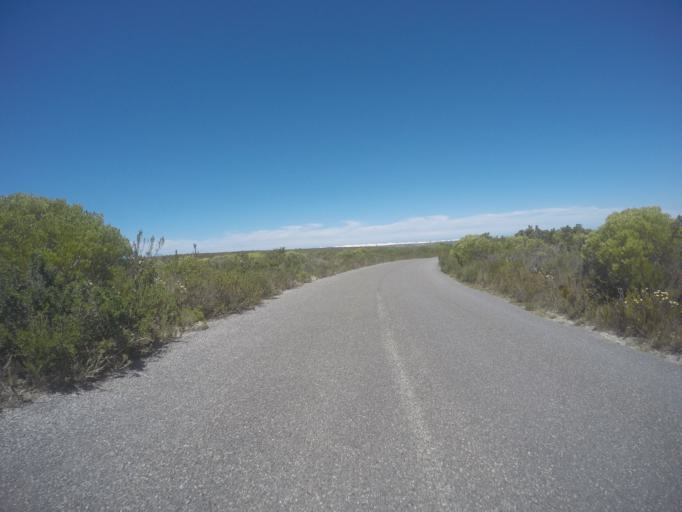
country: ZA
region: Western Cape
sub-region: Overberg District Municipality
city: Bredasdorp
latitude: -34.4301
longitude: 20.4174
